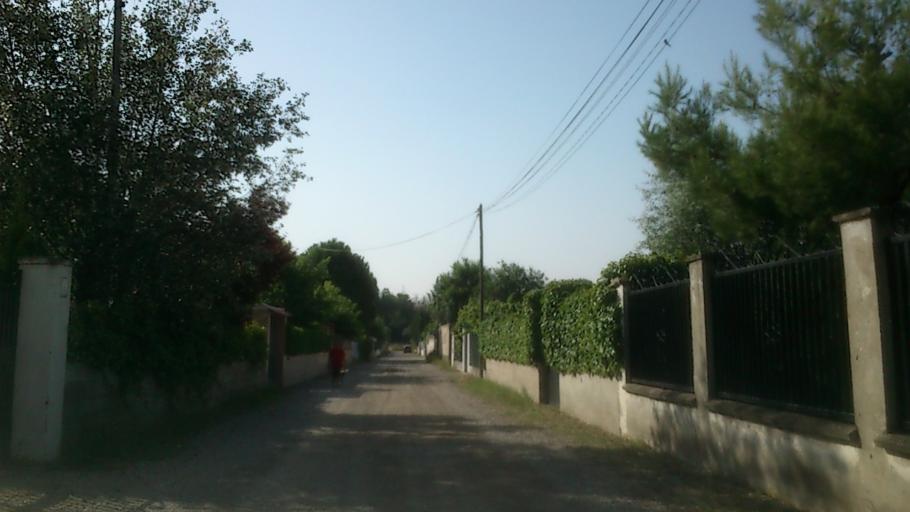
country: ES
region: Aragon
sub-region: Provincia de Zaragoza
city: Villanueva de Gallego
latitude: 41.7615
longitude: -0.8029
